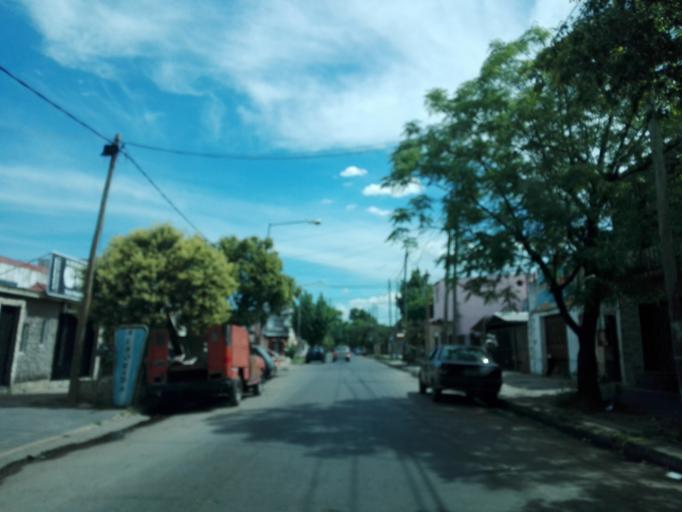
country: AR
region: Buenos Aires
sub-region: Partido de Lanus
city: Lanus
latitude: -34.7221
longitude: -58.3867
